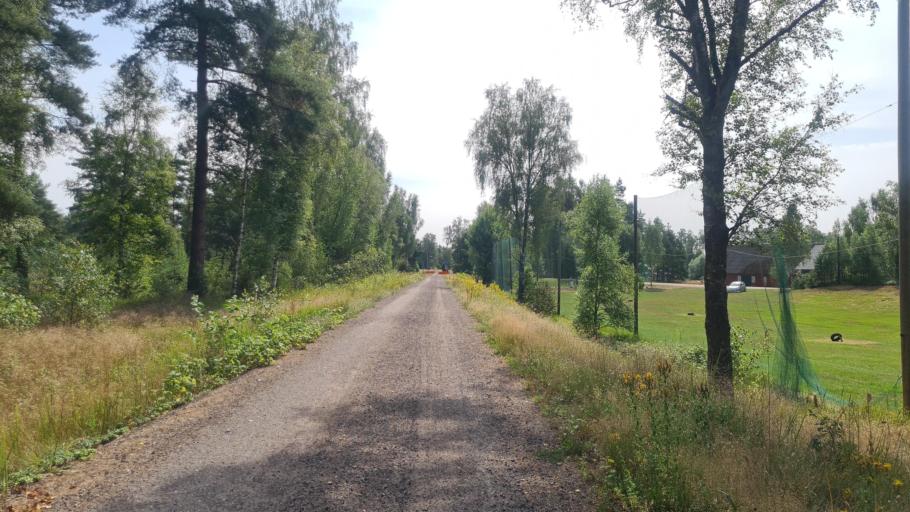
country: SE
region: Kronoberg
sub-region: Ljungby Kommun
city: Lagan
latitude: 56.9239
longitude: 13.9855
